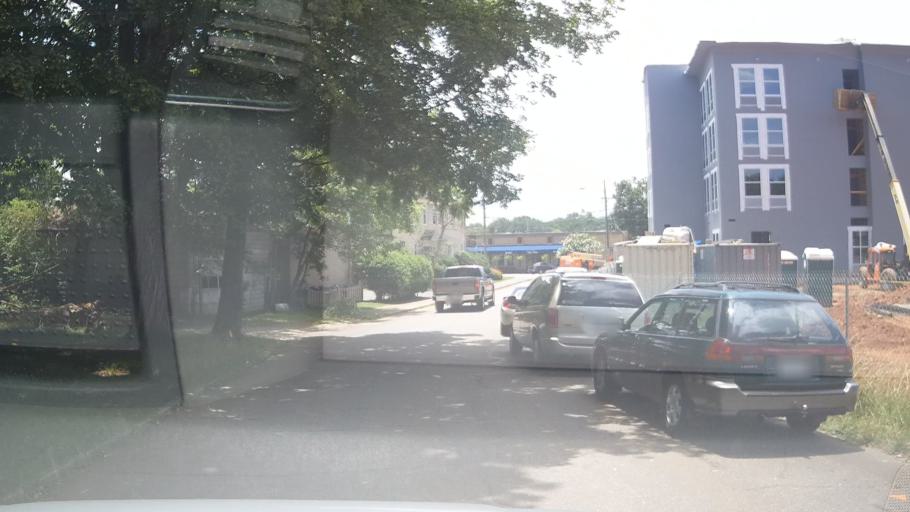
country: US
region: North Carolina
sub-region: Burke County
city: Morganton
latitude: 35.7486
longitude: -81.6908
